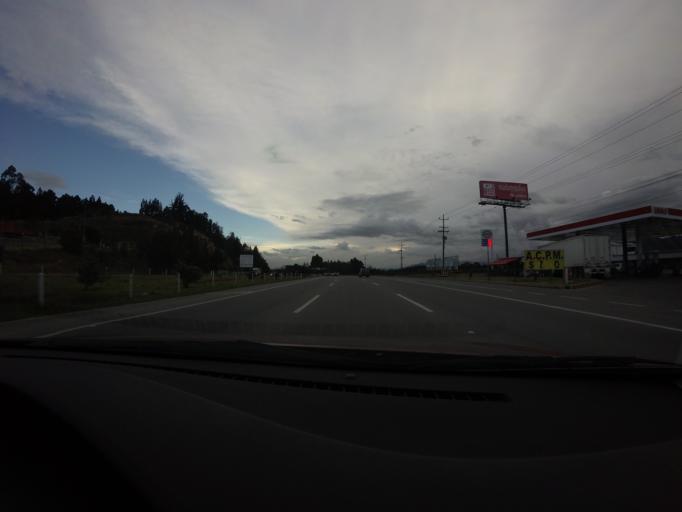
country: CO
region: Cundinamarca
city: Cajica
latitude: 4.9352
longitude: -73.9877
